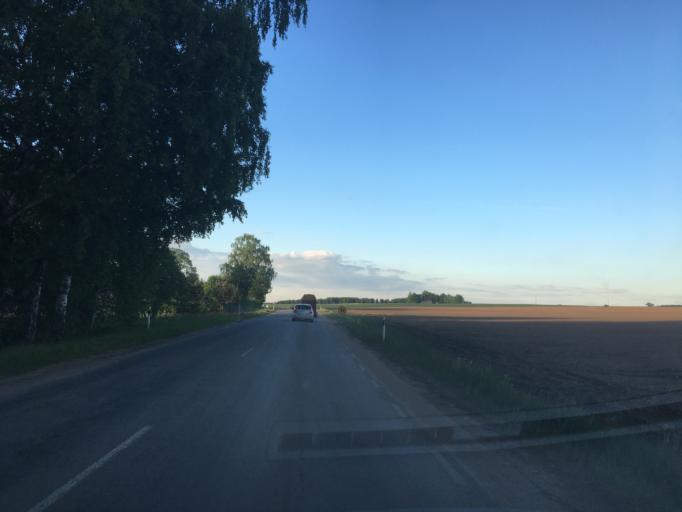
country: EE
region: Tartu
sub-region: UElenurme vald
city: Ulenurme
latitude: 58.2418
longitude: 26.6657
